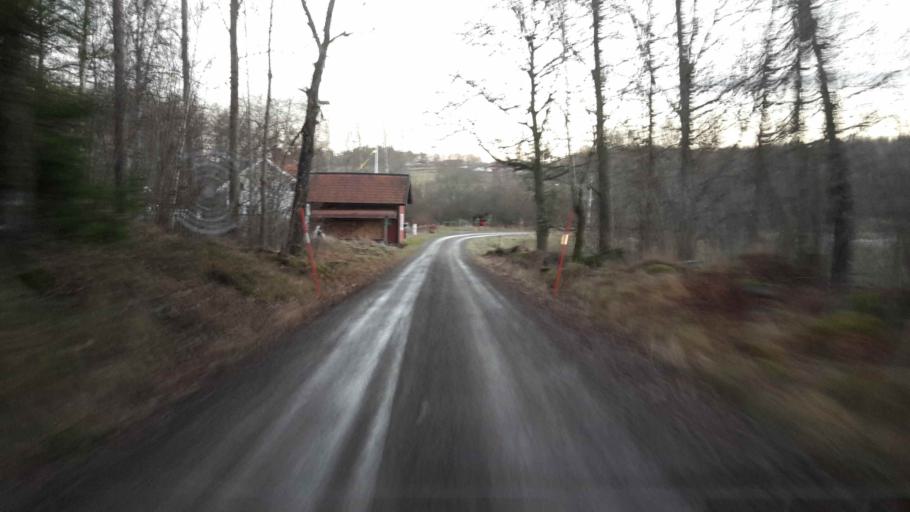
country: SE
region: OEstergoetland
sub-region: Atvidabergs Kommun
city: Atvidaberg
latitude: 58.2437
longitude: 16.0785
